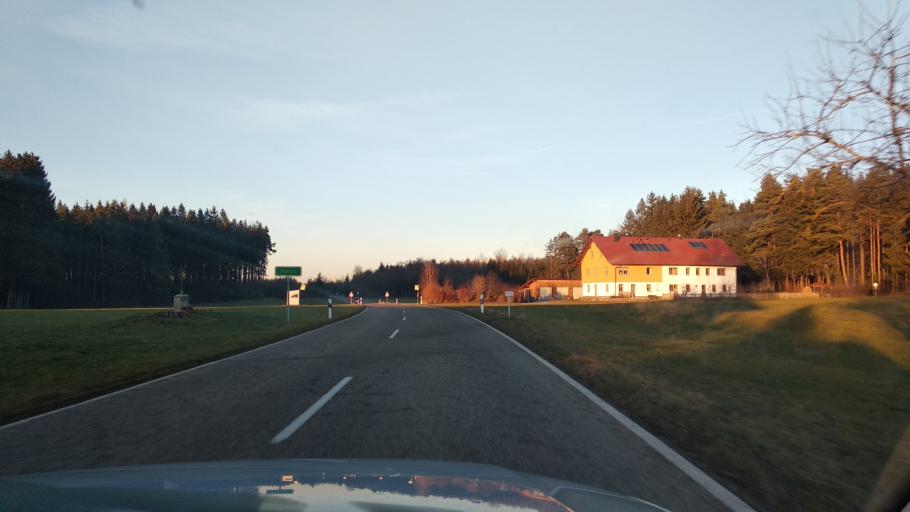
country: DE
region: Bavaria
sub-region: Swabia
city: Kronburg
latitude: 47.9204
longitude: 10.1530
